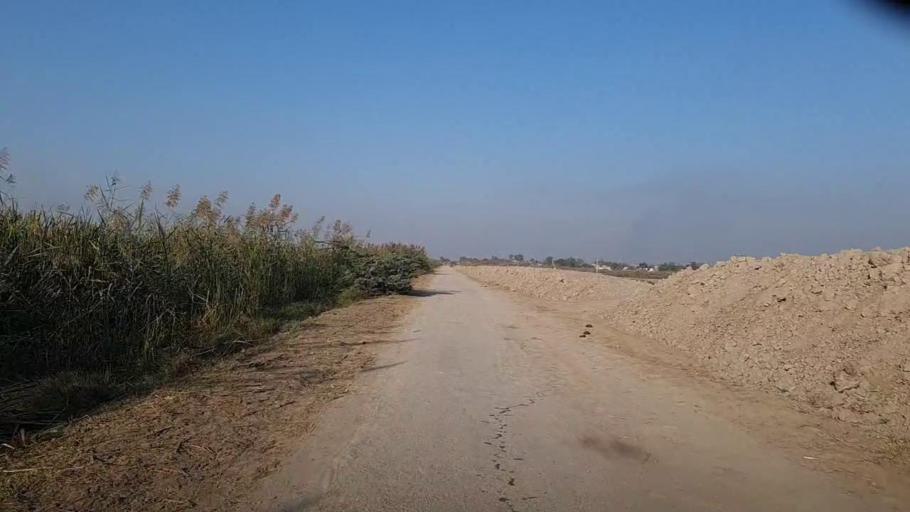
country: PK
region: Sindh
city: Ranipur
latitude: 27.2538
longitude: 68.5087
